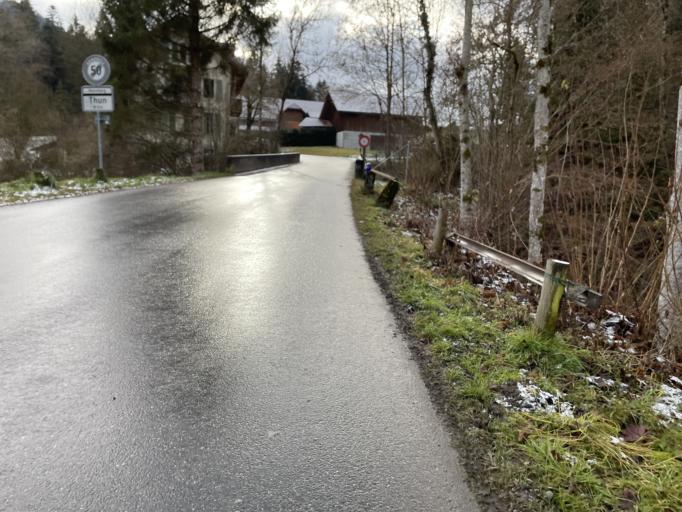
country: CH
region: Bern
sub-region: Thun District
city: Heimberg
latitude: 46.8096
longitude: 7.6127
